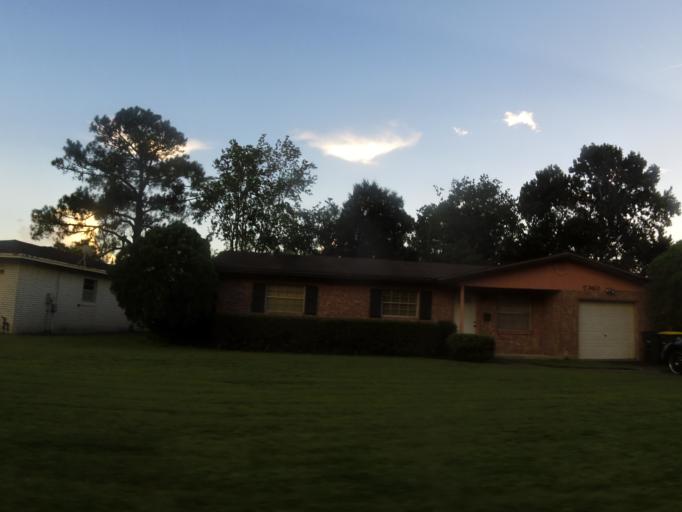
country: US
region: Florida
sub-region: Duval County
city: Jacksonville
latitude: 30.2393
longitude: -81.6041
